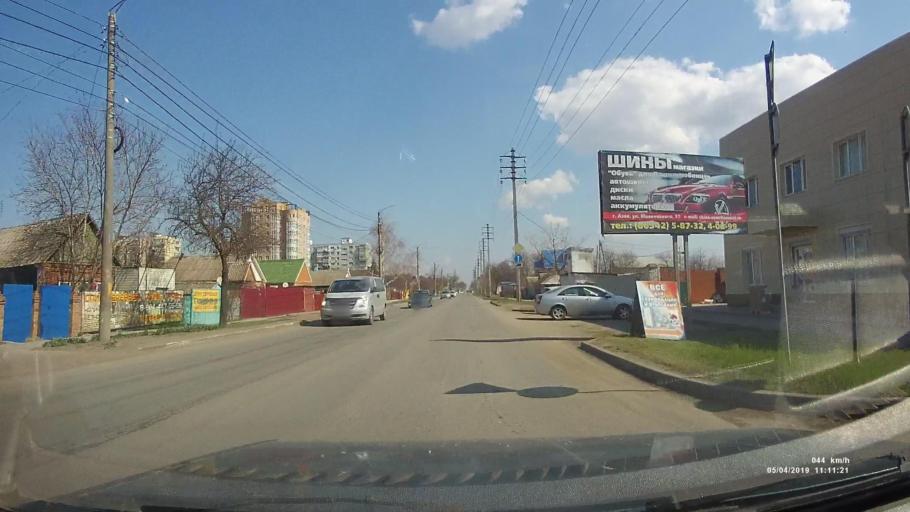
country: RU
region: Rostov
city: Azov
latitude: 47.0945
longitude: 39.4343
